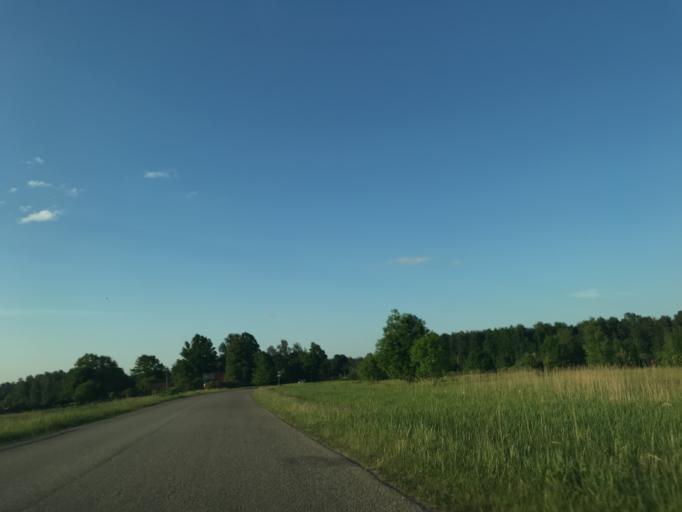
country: LV
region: Baldone
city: Baldone
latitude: 56.7122
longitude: 24.3685
